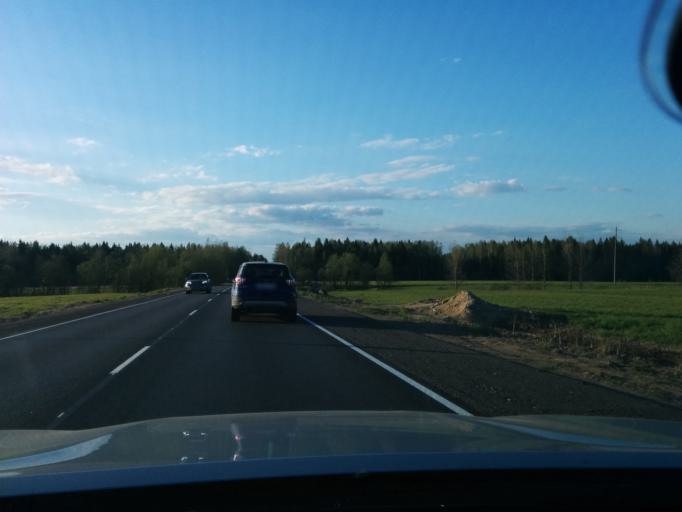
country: RU
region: Leningrad
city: Verkhniye Osel'ki
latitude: 60.2025
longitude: 30.4264
